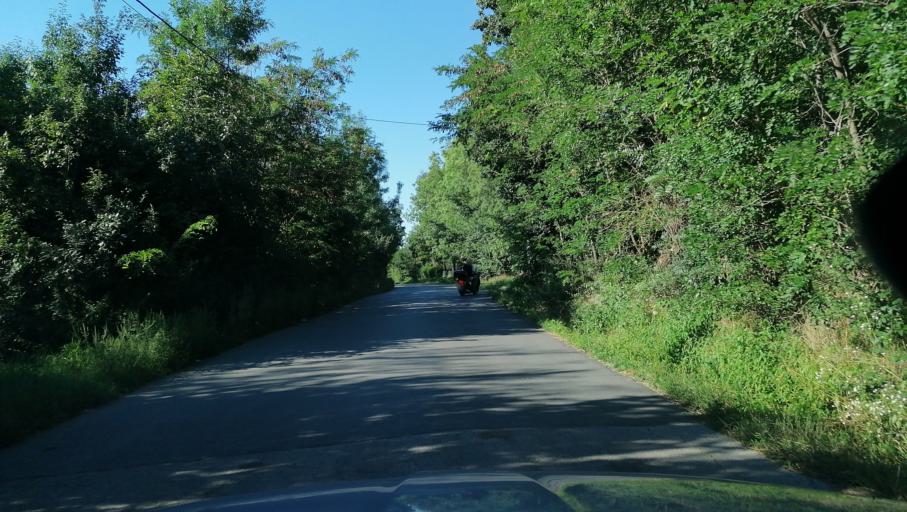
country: RS
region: Central Serbia
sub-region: Sumadijski Okrug
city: Knic
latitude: 43.8477
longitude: 20.6037
